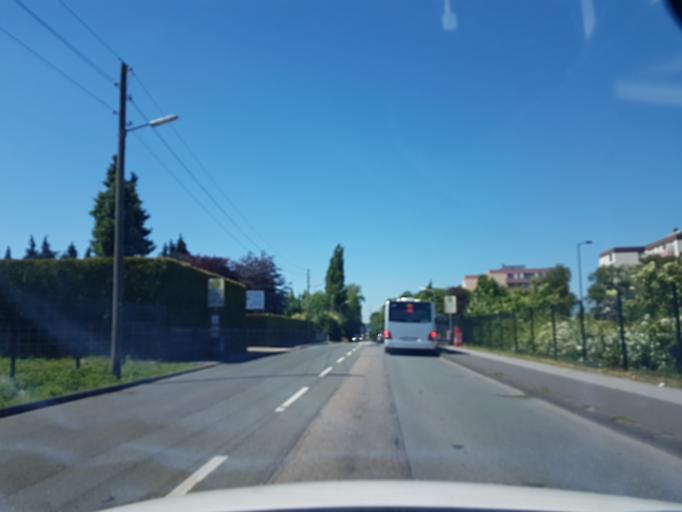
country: DE
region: North Rhine-Westphalia
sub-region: Regierungsbezirk Dusseldorf
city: Ratingen
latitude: 51.3456
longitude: 6.8354
